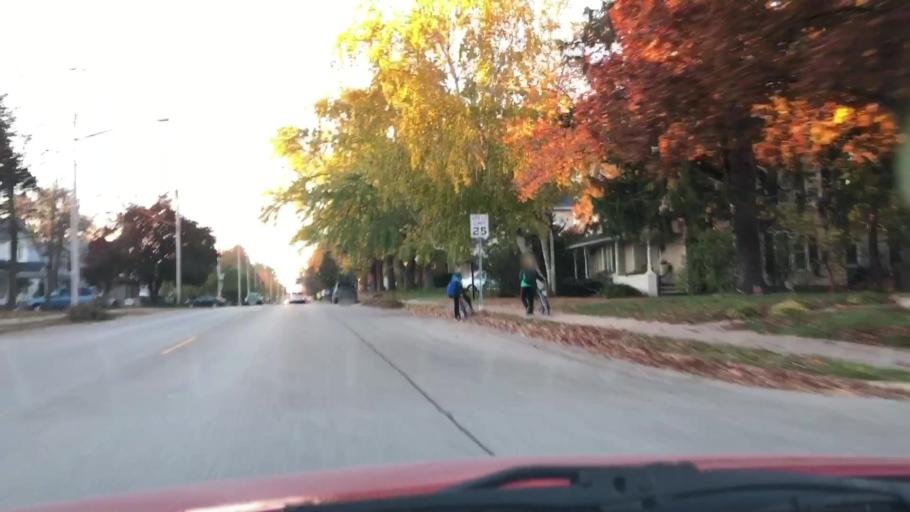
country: US
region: Wisconsin
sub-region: Outagamie County
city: Seymour
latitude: 44.5078
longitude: -88.3305
